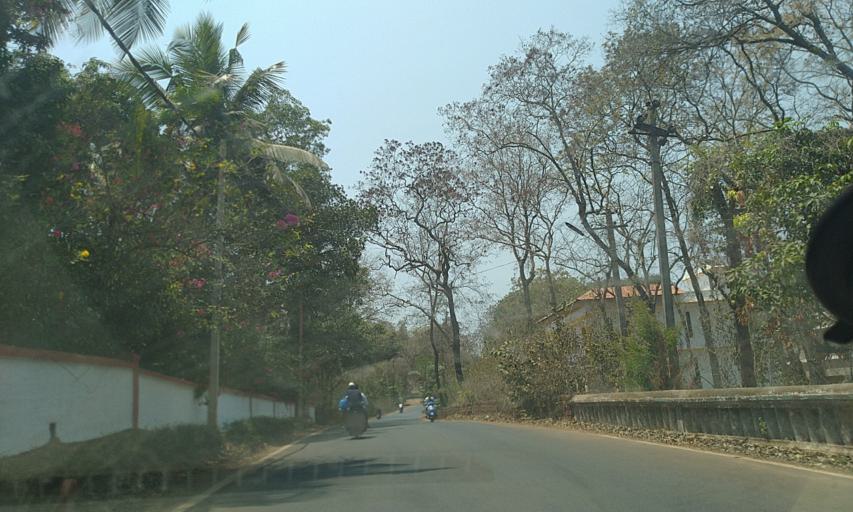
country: IN
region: Goa
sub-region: North Goa
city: Solim
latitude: 15.5972
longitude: 73.7845
